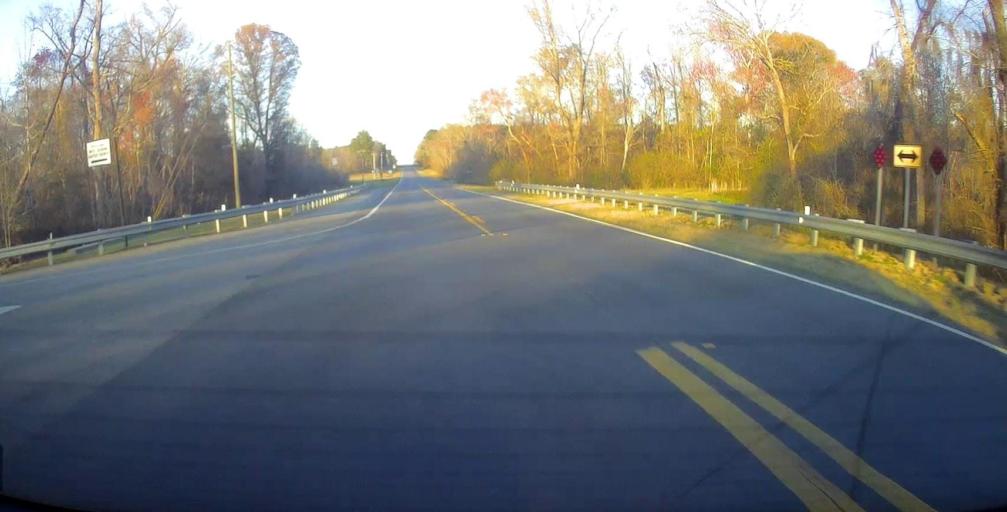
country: US
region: Georgia
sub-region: Laurens County
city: Dublin
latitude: 32.4040
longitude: -82.9683
